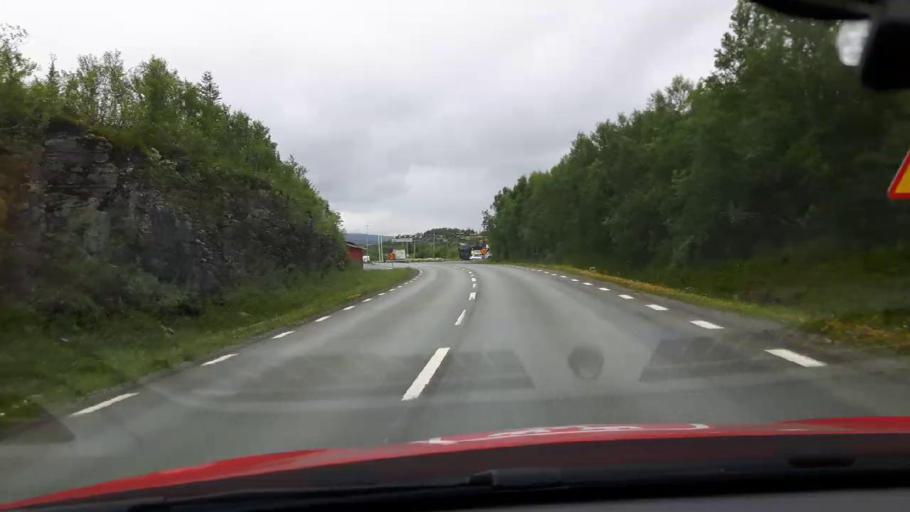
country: NO
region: Nord-Trondelag
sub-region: Meraker
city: Meraker
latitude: 63.3169
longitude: 12.0932
